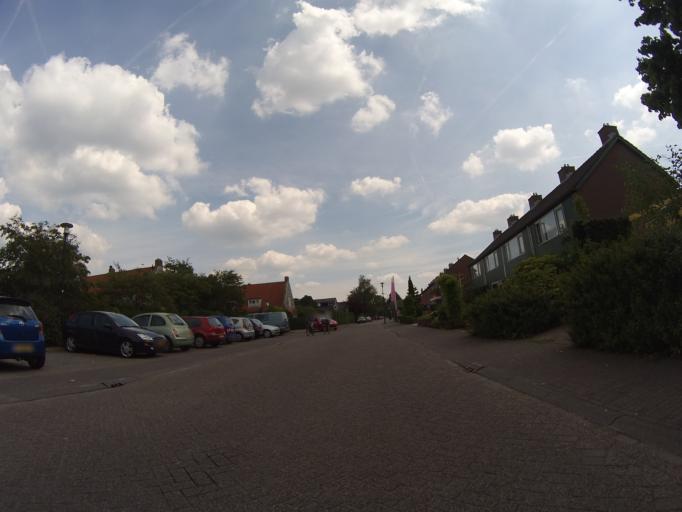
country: NL
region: Utrecht
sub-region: Gemeente De Bilt
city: De Bilt
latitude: 52.1552
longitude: 5.1770
